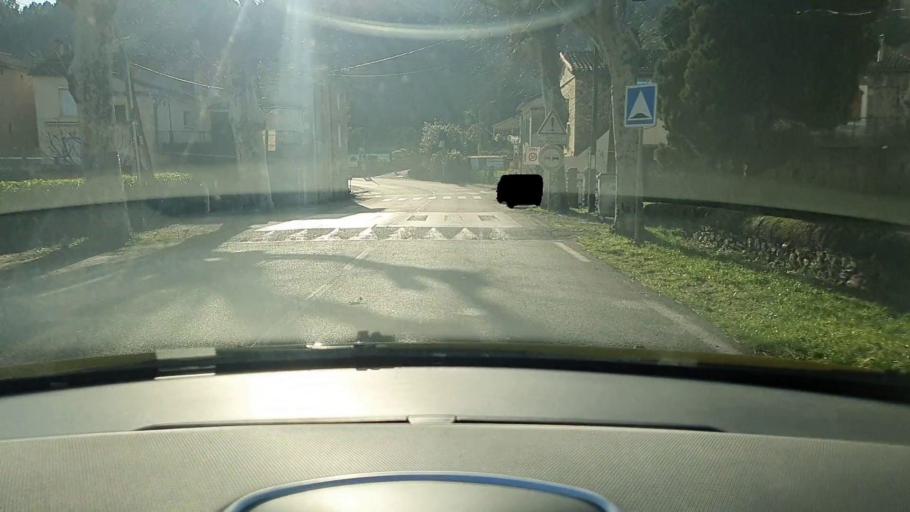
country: FR
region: Languedoc-Roussillon
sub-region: Departement du Gard
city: Branoux-les-Taillades
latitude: 44.3065
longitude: 3.9706
